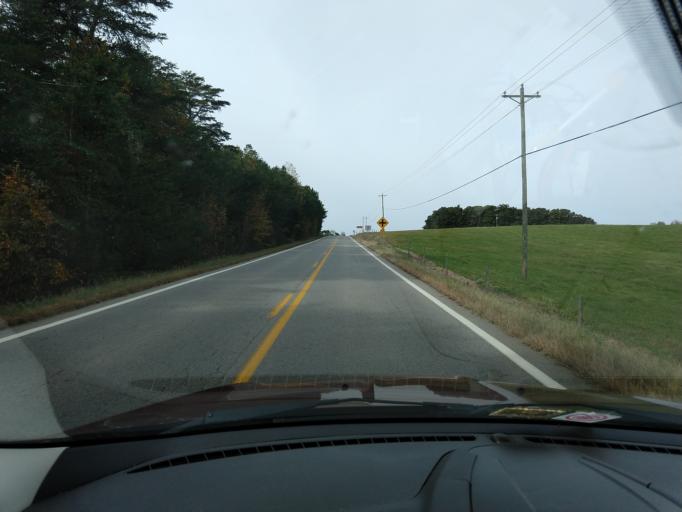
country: US
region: Virginia
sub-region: Pittsylvania County
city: Gretna
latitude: 36.9544
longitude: -79.4152
